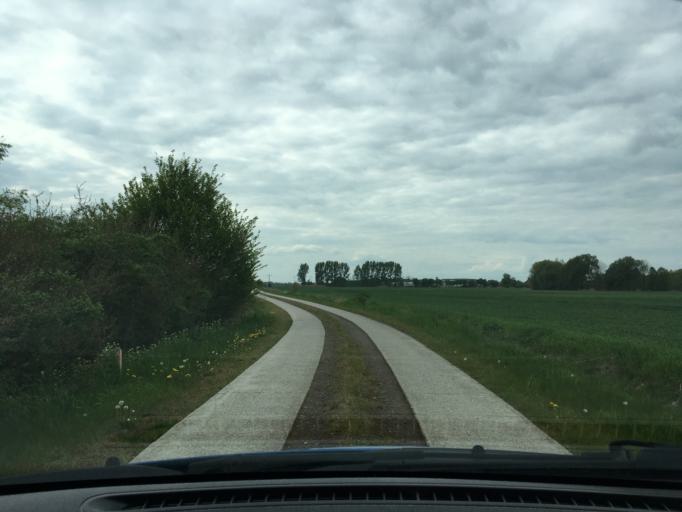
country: DE
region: Lower Saxony
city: Neu Darchau
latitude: 53.2790
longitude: 10.9242
